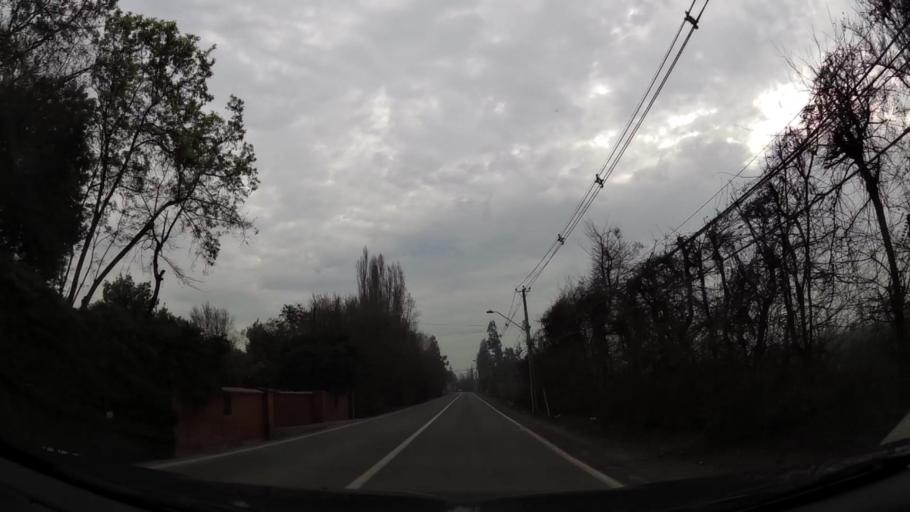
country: CL
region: Santiago Metropolitan
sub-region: Provincia de Chacabuco
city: Chicureo Abajo
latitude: -33.2495
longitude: -70.7637
